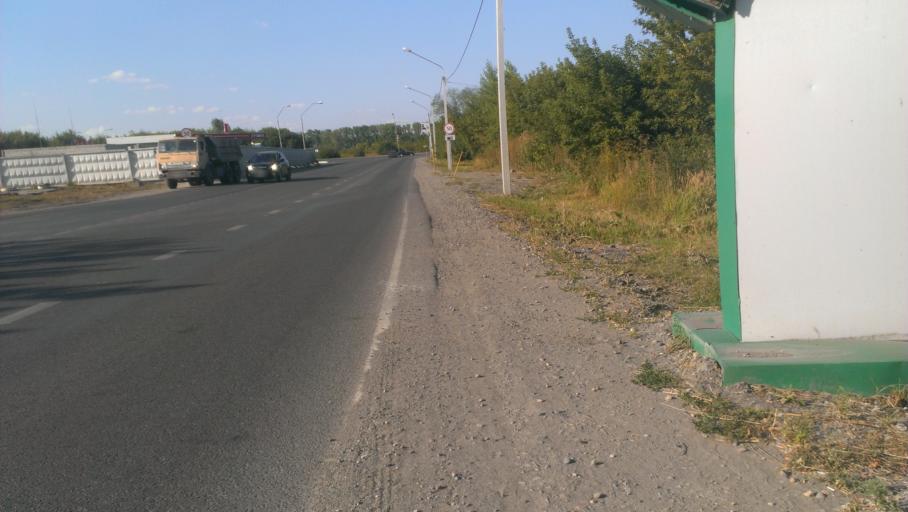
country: RU
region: Altai Krai
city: Novosilikatnyy
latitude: 53.3476
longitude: 83.6203
